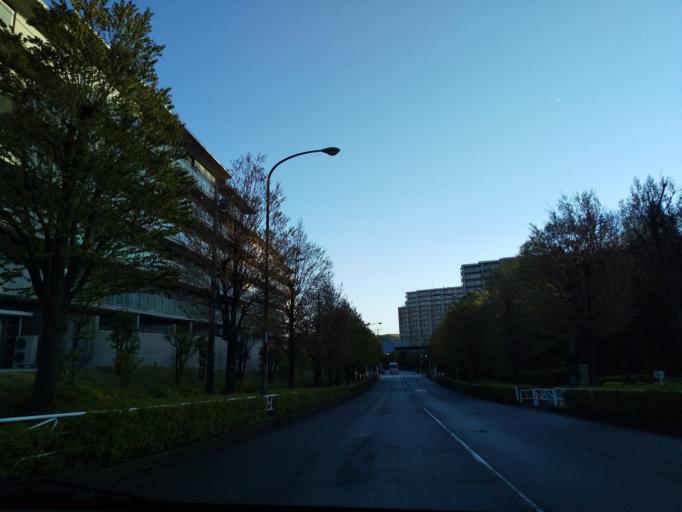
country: JP
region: Tokyo
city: Hino
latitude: 35.6190
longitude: 139.3761
